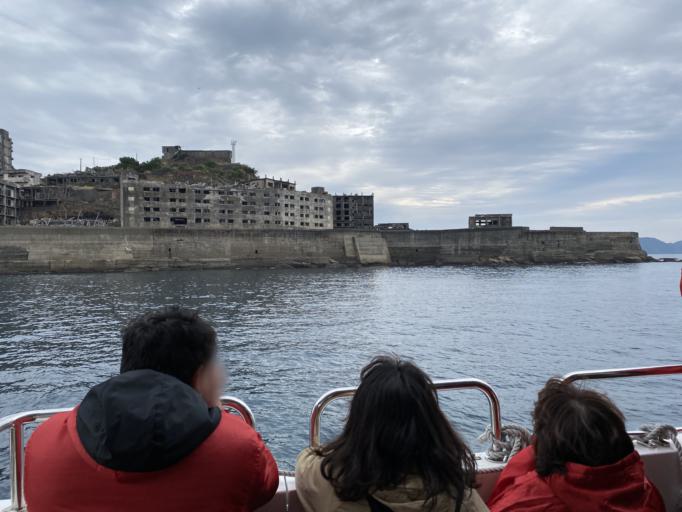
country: JP
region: Nagasaki
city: Nagasaki-shi
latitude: 32.6281
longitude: 129.7358
